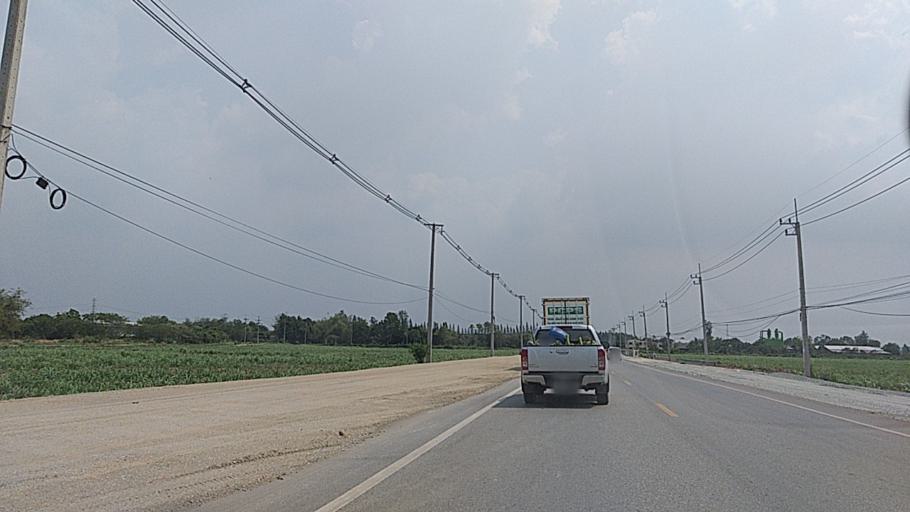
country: TH
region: Chon Buri
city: Phanat Nikhom
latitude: 13.3671
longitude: 101.1960
